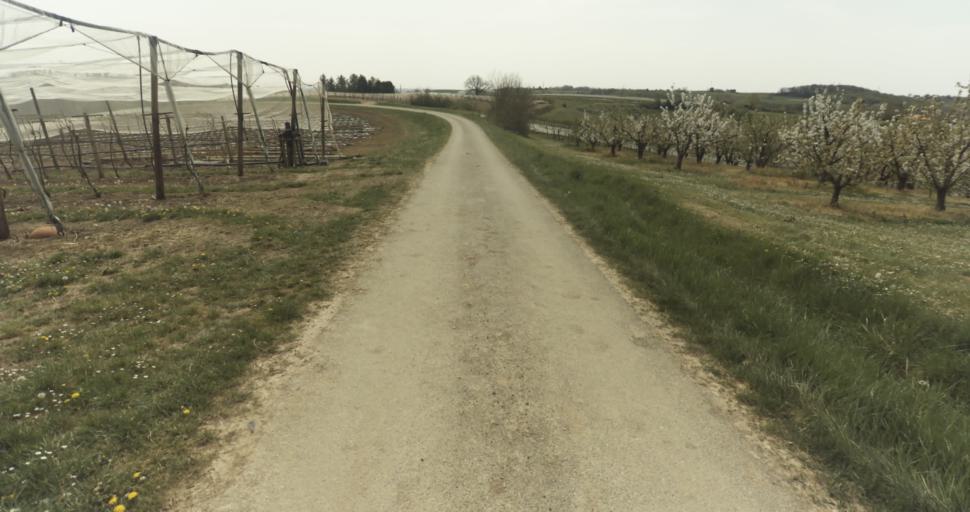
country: FR
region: Midi-Pyrenees
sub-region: Departement du Tarn-et-Garonne
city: Moissac
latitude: 44.1188
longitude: 1.0543
